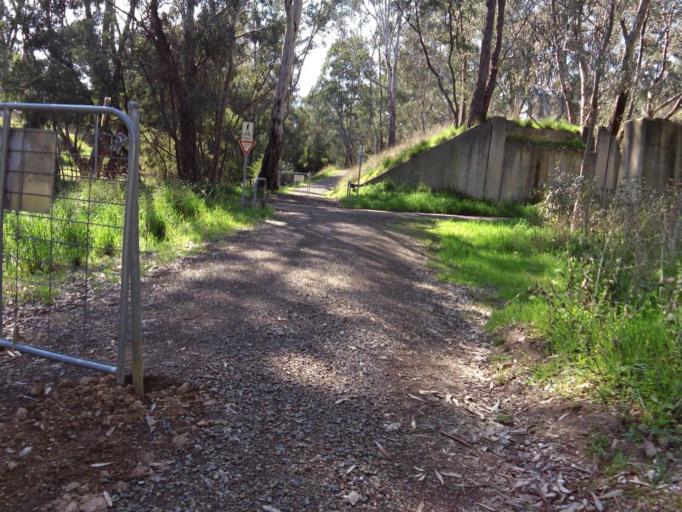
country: AU
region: Victoria
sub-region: Murrindindi
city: Alexandra
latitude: -37.1616
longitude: 145.5602
